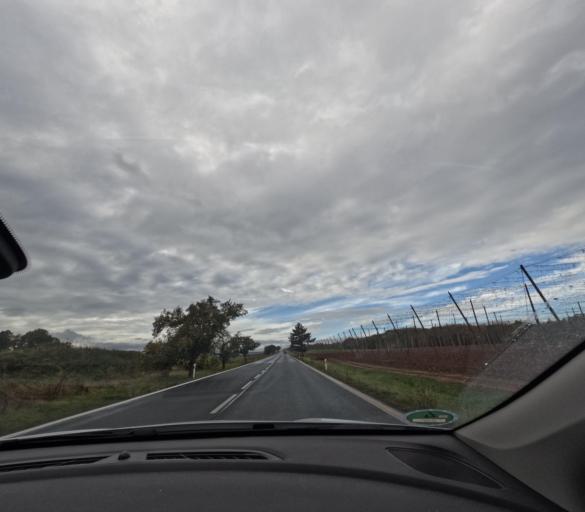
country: CZ
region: Ustecky
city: Kryry
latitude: 50.1350
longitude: 13.4254
